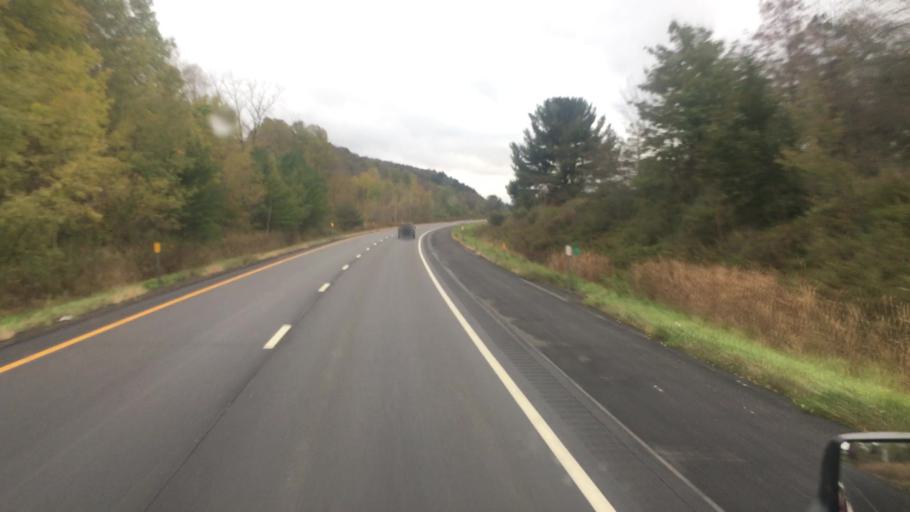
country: US
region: New York
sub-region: Chenango County
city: Bainbridge
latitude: 42.2903
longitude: -75.4396
